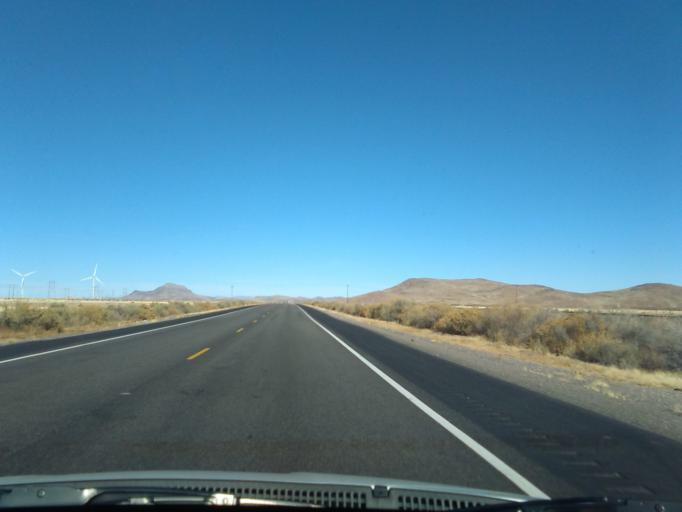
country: US
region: New Mexico
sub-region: Luna County
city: Deming
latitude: 32.5151
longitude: -107.5014
